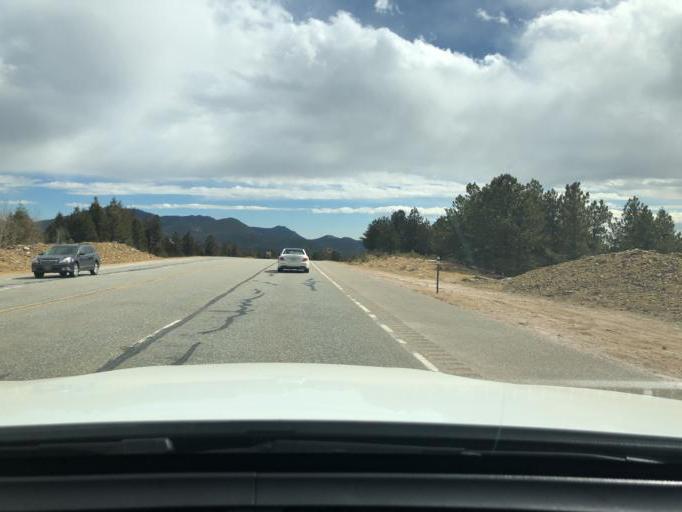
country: US
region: Colorado
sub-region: Gilpin County
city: Central City
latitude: 39.7892
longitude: -105.5019
